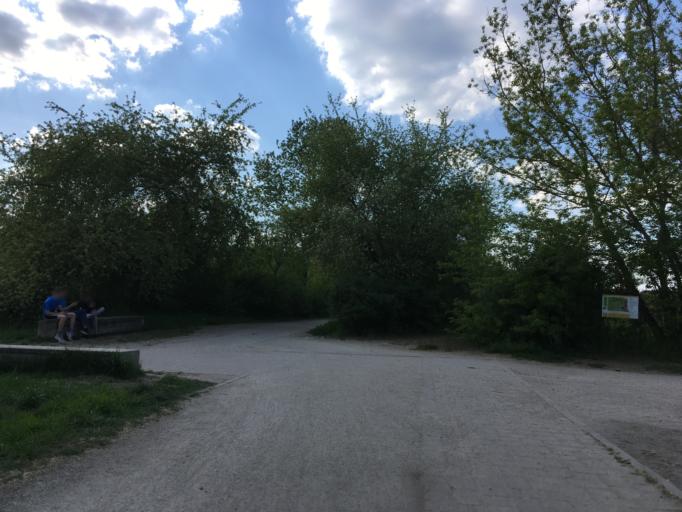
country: DE
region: Berlin
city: Falkenberg
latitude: 52.5746
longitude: 13.5413
